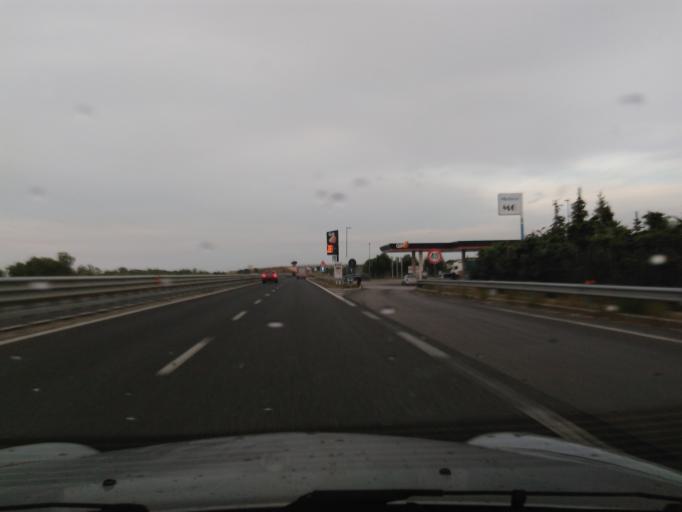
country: IT
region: Apulia
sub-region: Provincia di Bari
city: Giovinazzo
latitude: 41.1736
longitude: 16.6837
